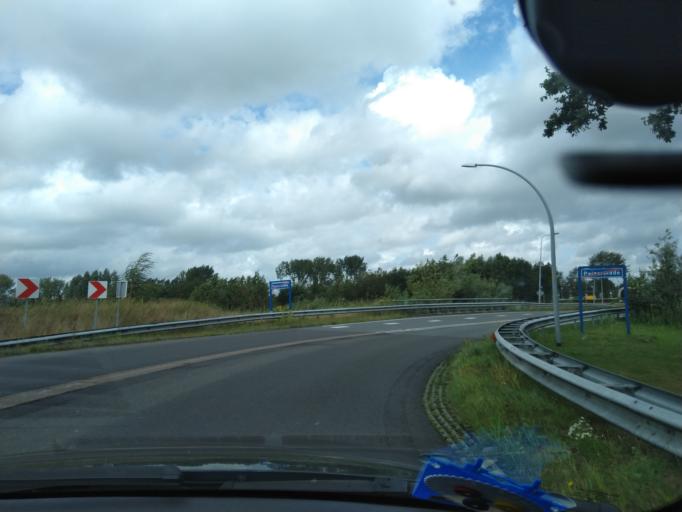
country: NL
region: Groningen
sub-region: Gemeente Groningen
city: Groningen
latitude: 53.1964
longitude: 6.5114
